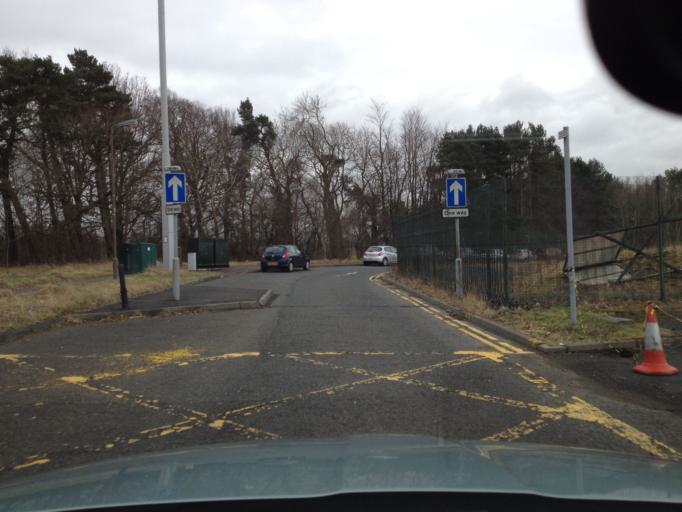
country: GB
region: Scotland
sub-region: West Lothian
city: West Calder
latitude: 55.8800
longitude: -3.5495
